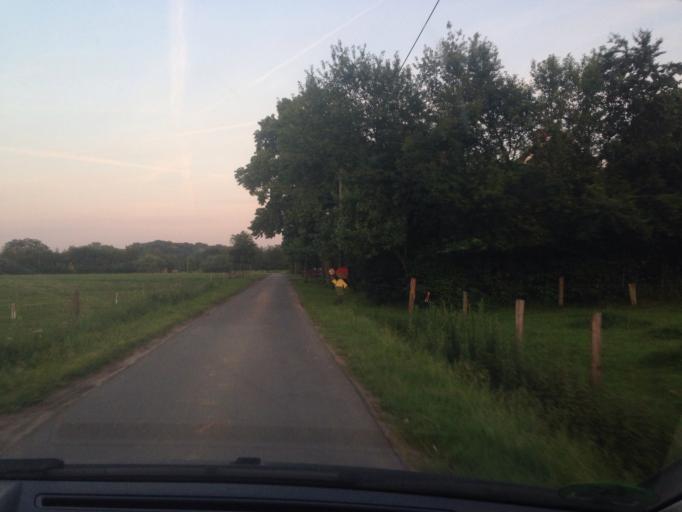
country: DE
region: North Rhine-Westphalia
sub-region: Regierungsbezirk Munster
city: Greven
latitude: 52.0199
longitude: 7.5512
